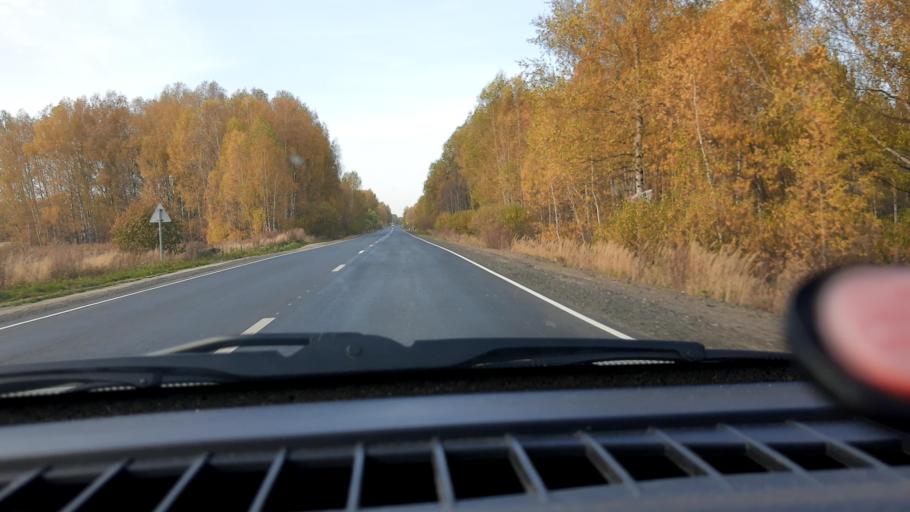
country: RU
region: Nizjnij Novgorod
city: Lukino
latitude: 56.5334
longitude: 43.7972
